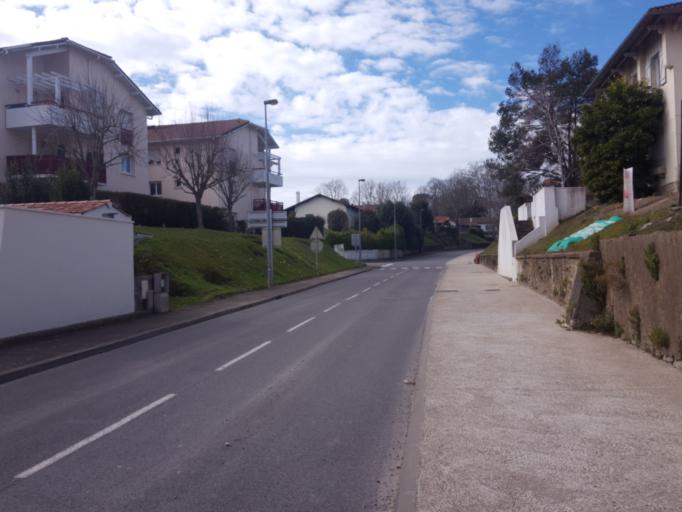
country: FR
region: Aquitaine
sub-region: Departement des Landes
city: Saint-Martin-de-Seignanx
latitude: 43.5447
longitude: -1.3868
